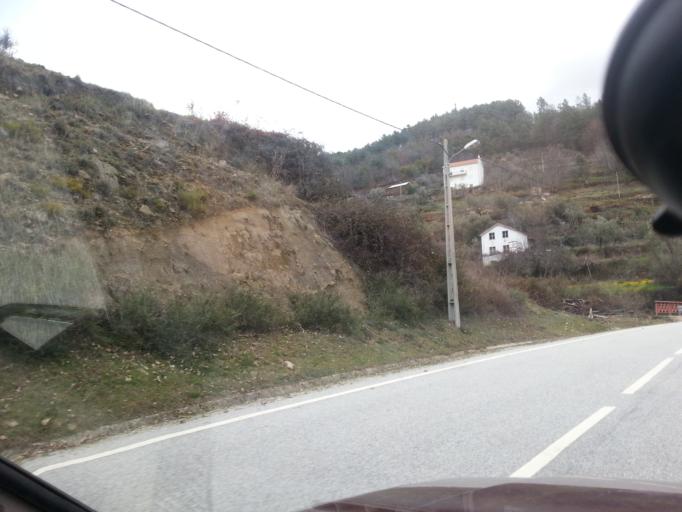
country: PT
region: Guarda
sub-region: Manteigas
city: Manteigas
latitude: 40.4069
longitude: -7.5350
